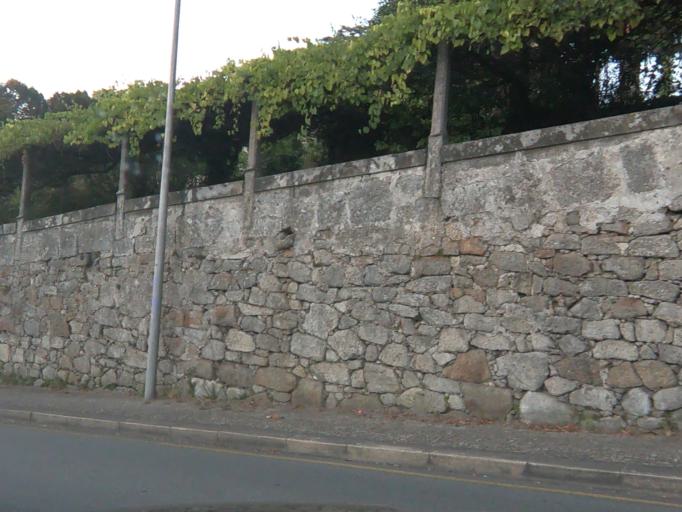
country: PT
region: Porto
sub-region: Gondomar
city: Valbom
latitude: 41.1430
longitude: -8.5725
